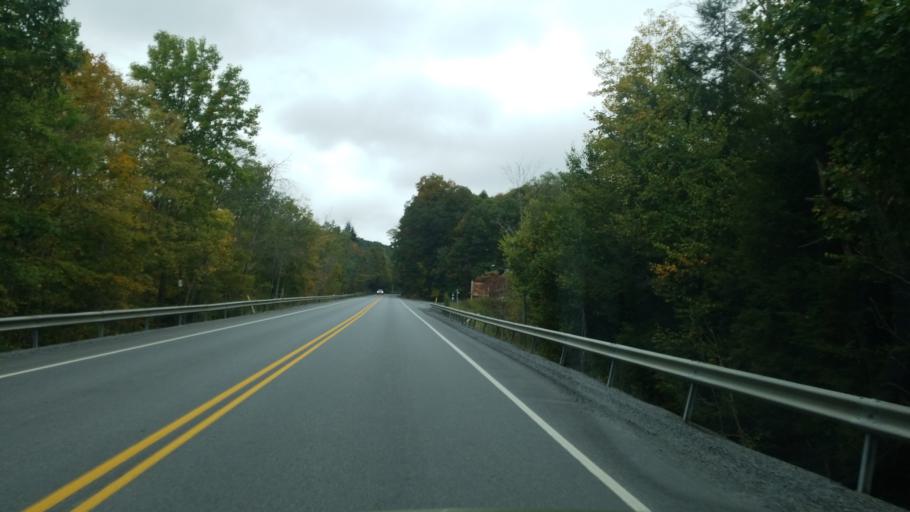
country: US
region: Pennsylvania
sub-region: Clearfield County
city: Curwensville
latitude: 40.9713
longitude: -78.5746
